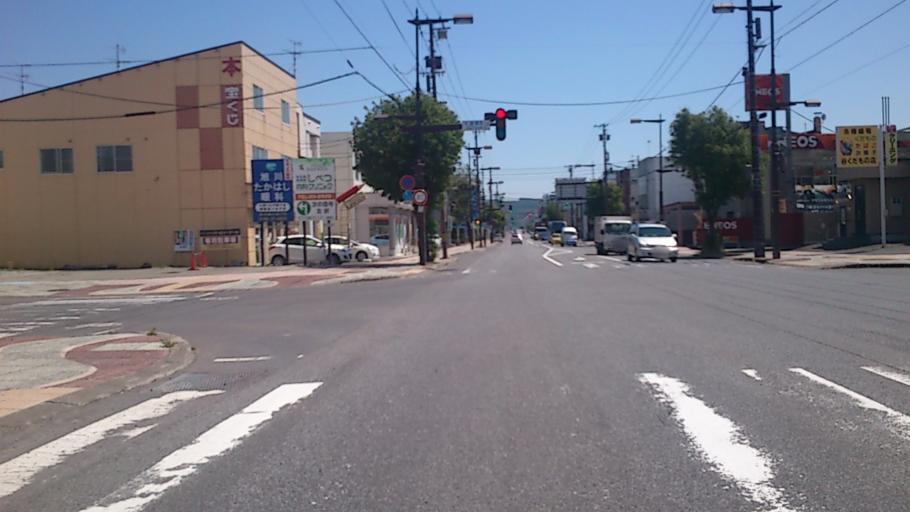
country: JP
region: Hokkaido
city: Nayoro
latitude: 44.1731
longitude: 142.3934
